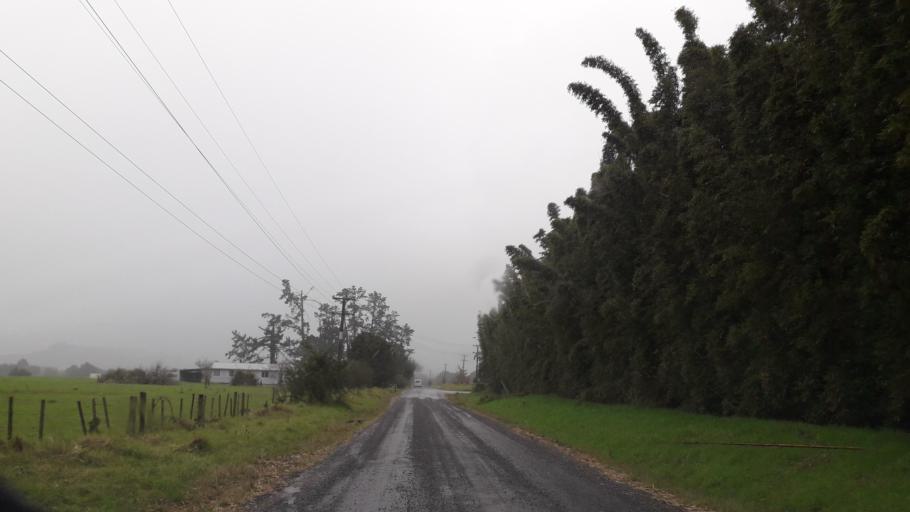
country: NZ
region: Northland
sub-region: Far North District
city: Waimate North
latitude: -35.4978
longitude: 173.6991
